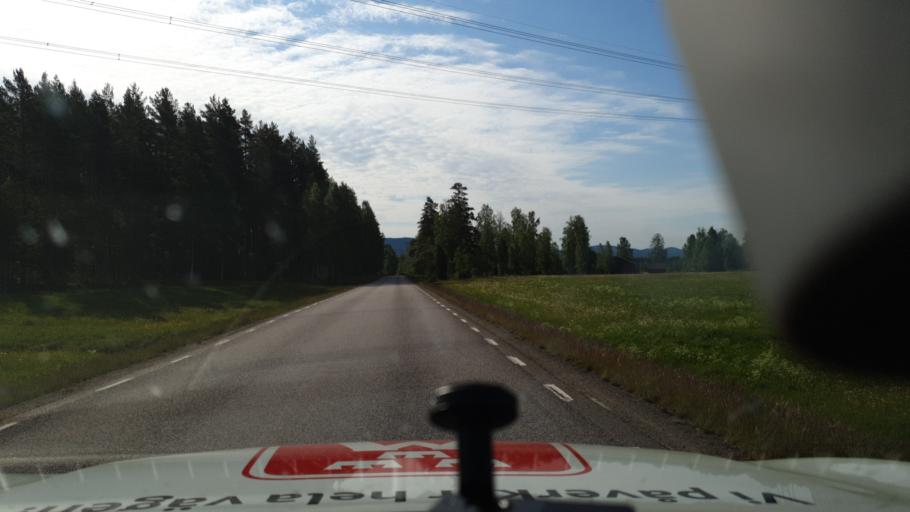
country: SE
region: Vaermland
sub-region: Torsby Kommun
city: Torsby
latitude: 59.9681
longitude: 12.8920
